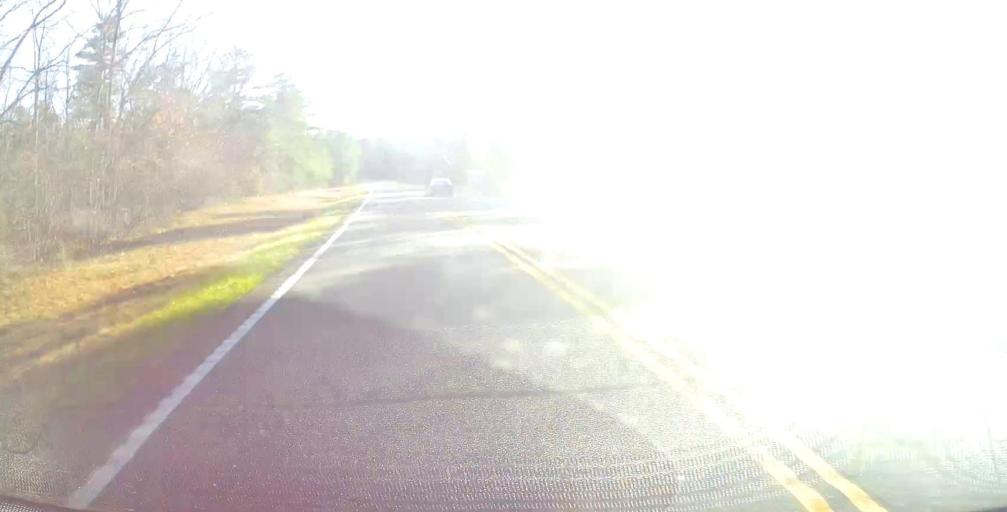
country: US
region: Georgia
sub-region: Meriwether County
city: Manchester
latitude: 32.8542
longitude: -84.6994
